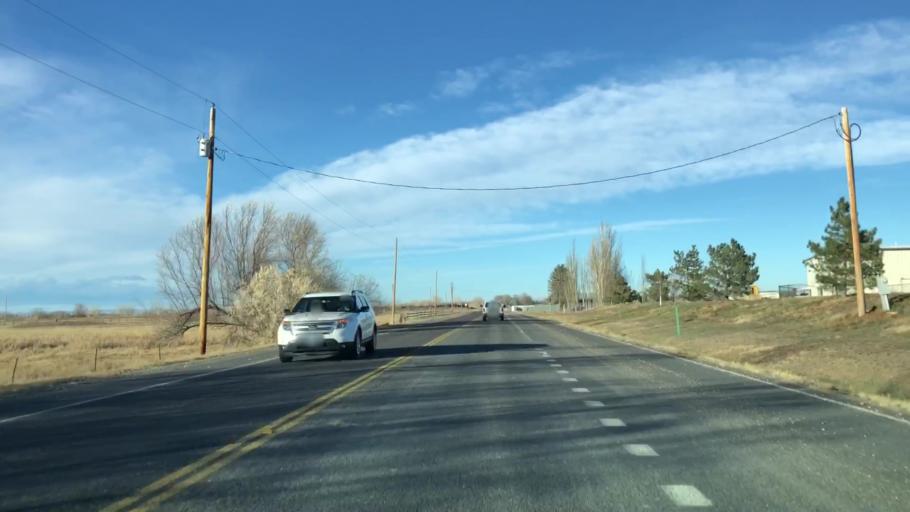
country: US
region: Colorado
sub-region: Weld County
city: Windsor
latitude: 40.4954
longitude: -104.9819
